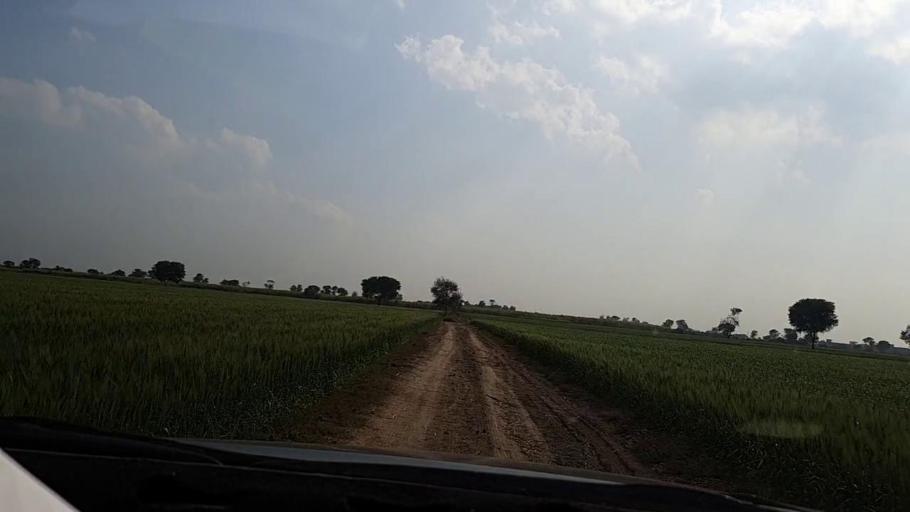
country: PK
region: Sindh
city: Nawabshah
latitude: 26.1674
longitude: 68.3661
